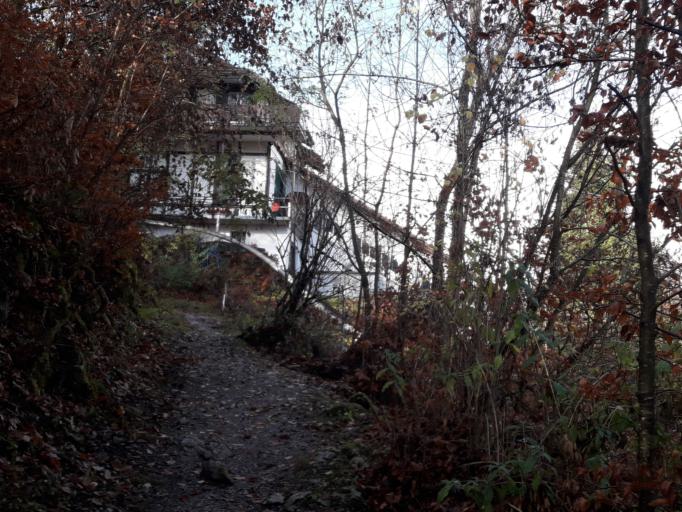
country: CH
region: Bern
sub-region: Interlaken-Oberhasli District
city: Unterseen
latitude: 46.6758
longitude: 7.8508
